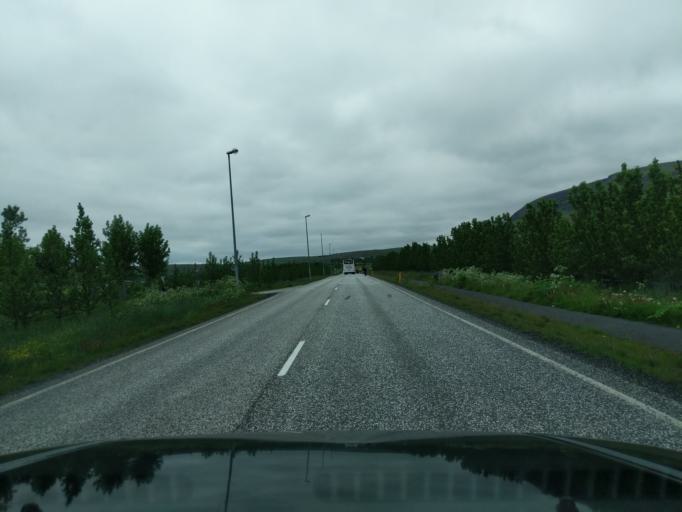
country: IS
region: Capital Region
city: Mosfellsbaer
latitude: 64.1811
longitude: -21.6079
